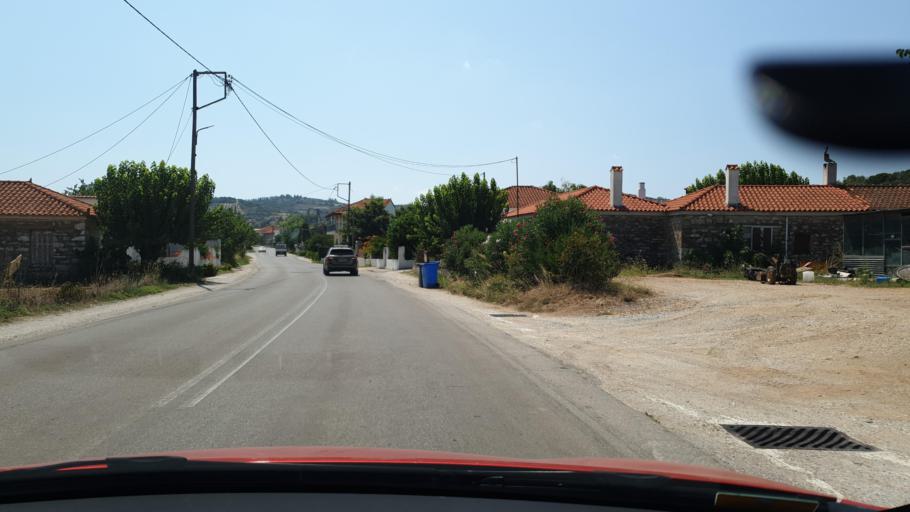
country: GR
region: Central Greece
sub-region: Nomos Evvoias
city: Aliveri
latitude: 38.4539
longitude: 24.1139
